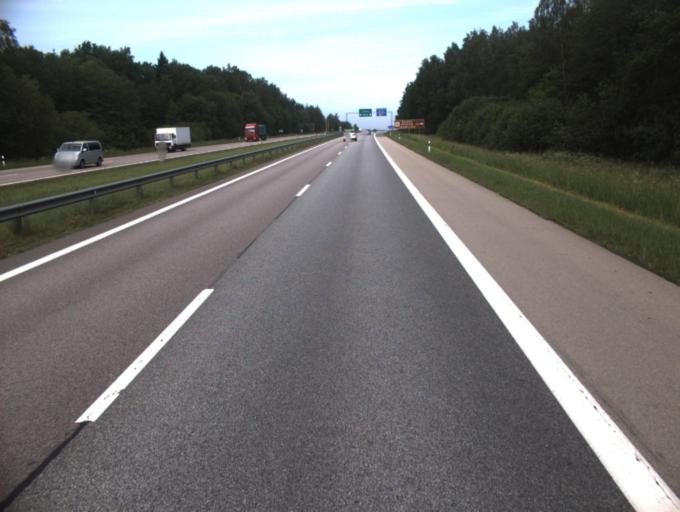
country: LT
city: Raseiniai
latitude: 55.3345
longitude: 23.1102
